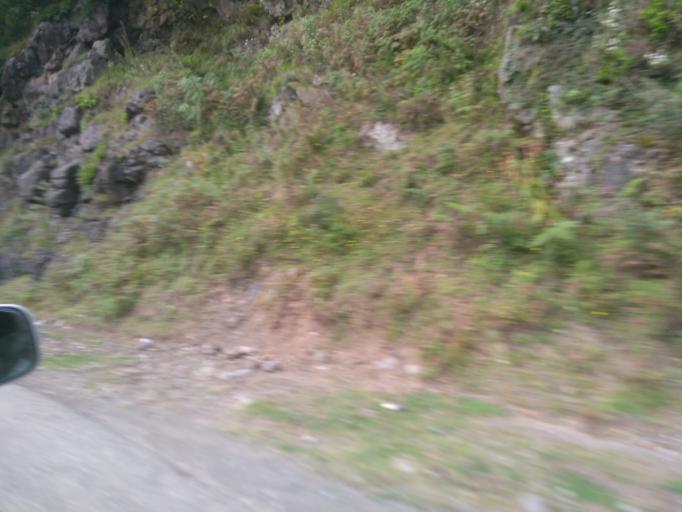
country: GE
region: Ajaria
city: Khelvachauri
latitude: 41.5451
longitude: 41.7133
